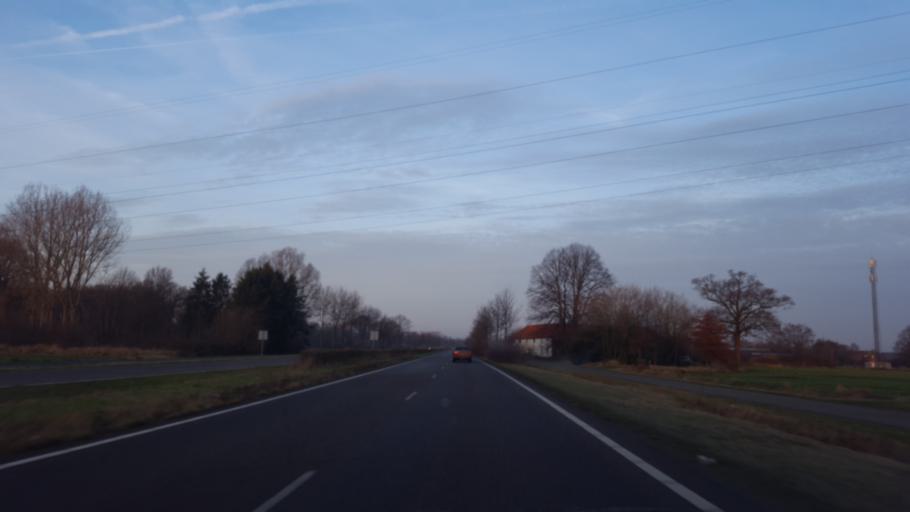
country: NL
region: Limburg
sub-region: Gemeente Weert
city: Weert
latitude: 51.2682
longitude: 5.6826
